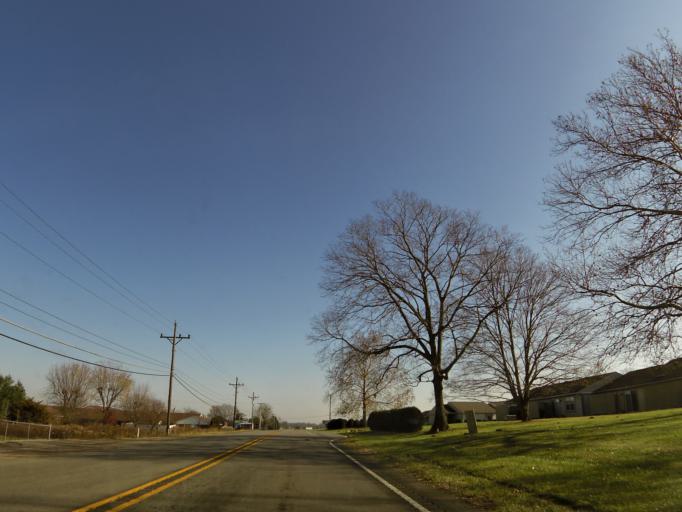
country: US
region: Indiana
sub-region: Fayette County
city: Connersville
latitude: 39.6389
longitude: -85.1042
